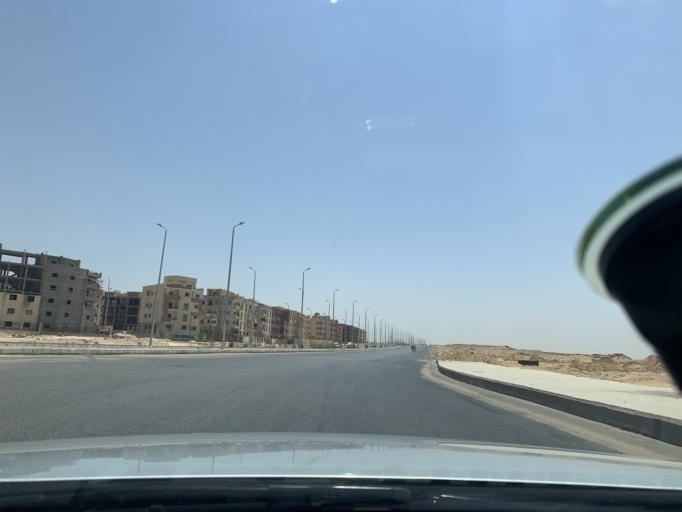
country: EG
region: Muhafazat al Qahirah
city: Cairo
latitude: 29.9984
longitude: 31.4686
